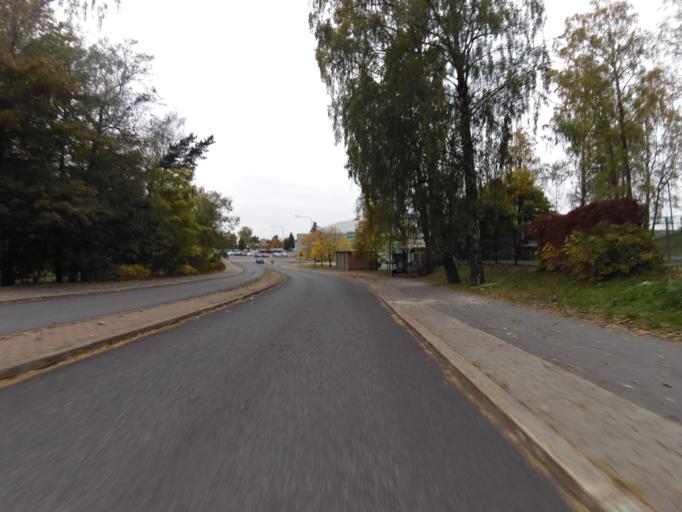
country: FI
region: Uusimaa
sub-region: Helsinki
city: Helsinki
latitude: 60.1856
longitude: 25.0014
